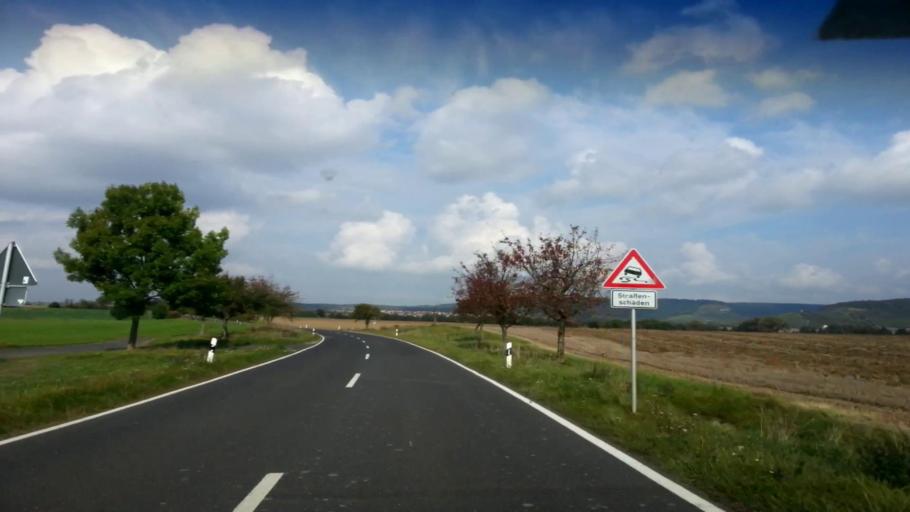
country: DE
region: Bavaria
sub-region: Regierungsbezirk Unterfranken
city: Oberschwarzach
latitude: 49.8451
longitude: 10.4066
